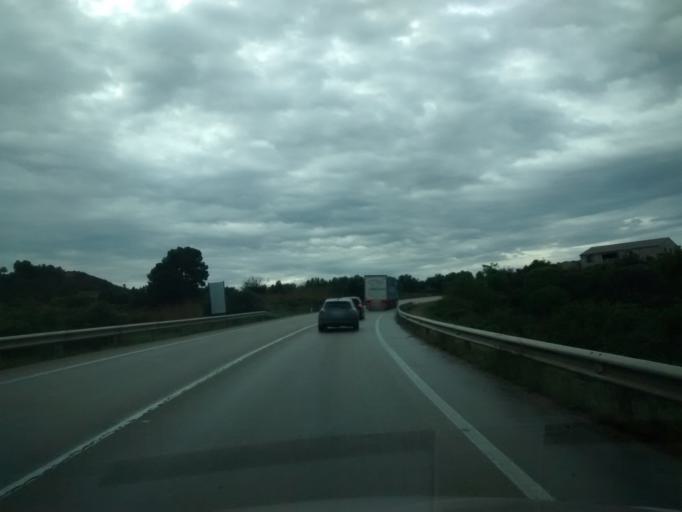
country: ES
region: Aragon
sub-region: Provincia de Zaragoza
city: Maella
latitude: 41.1307
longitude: 0.1271
